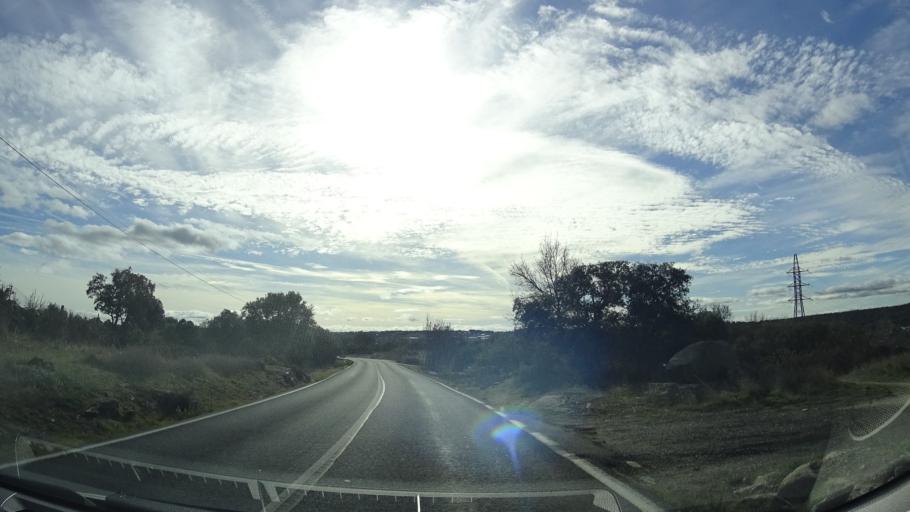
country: ES
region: Madrid
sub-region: Provincia de Madrid
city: Galapagar
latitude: 40.5958
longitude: -4.0024
